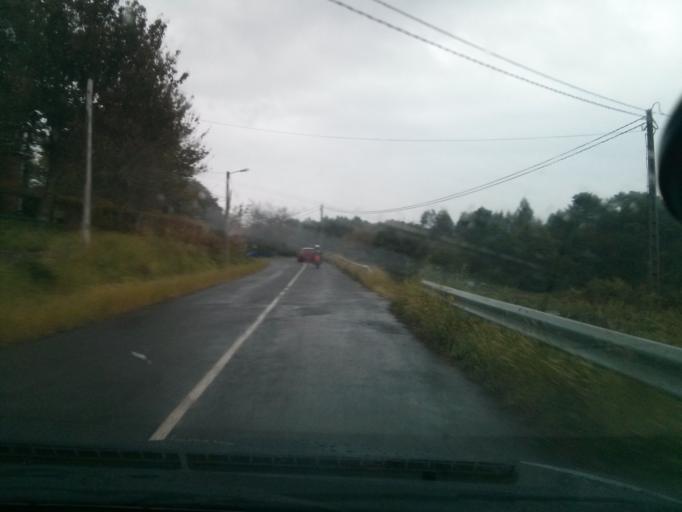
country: ES
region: Galicia
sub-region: Provincia da Coruna
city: Noia
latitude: 42.8197
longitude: -8.8853
